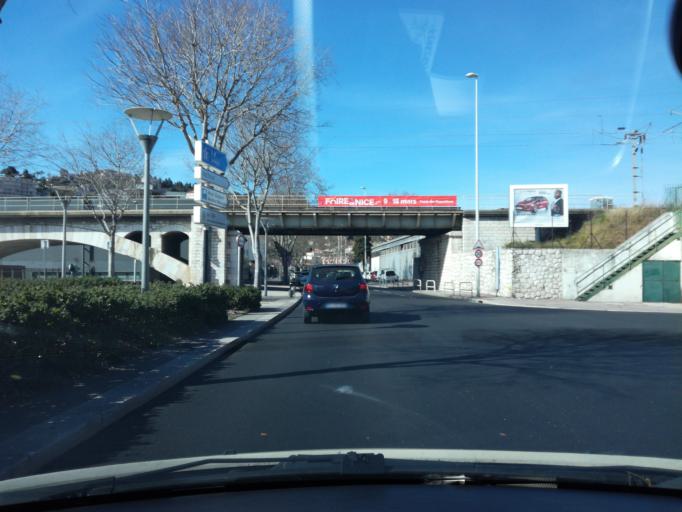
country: FR
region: Provence-Alpes-Cote d'Azur
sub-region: Departement des Alpes-Maritimes
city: Saint-Andre-de-la-Roche
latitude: 43.7140
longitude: 7.2836
